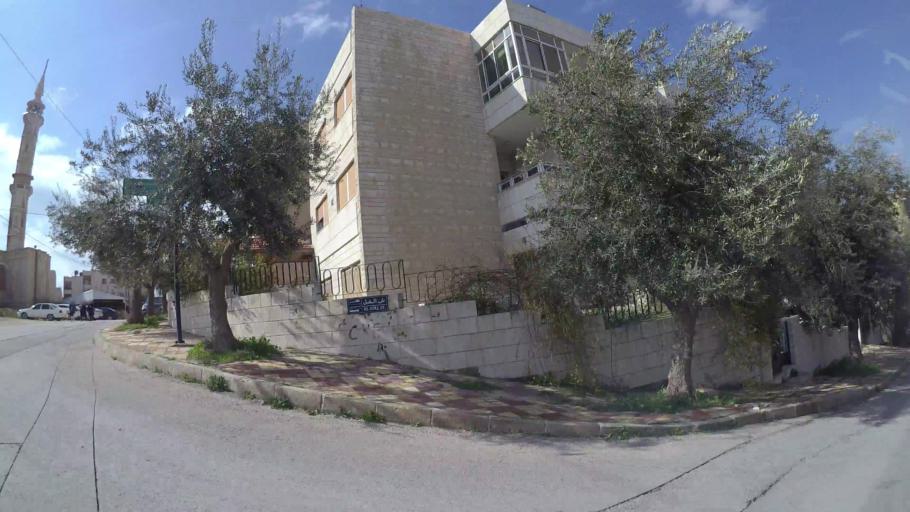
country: JO
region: Amman
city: Amman
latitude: 31.9748
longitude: 35.8932
